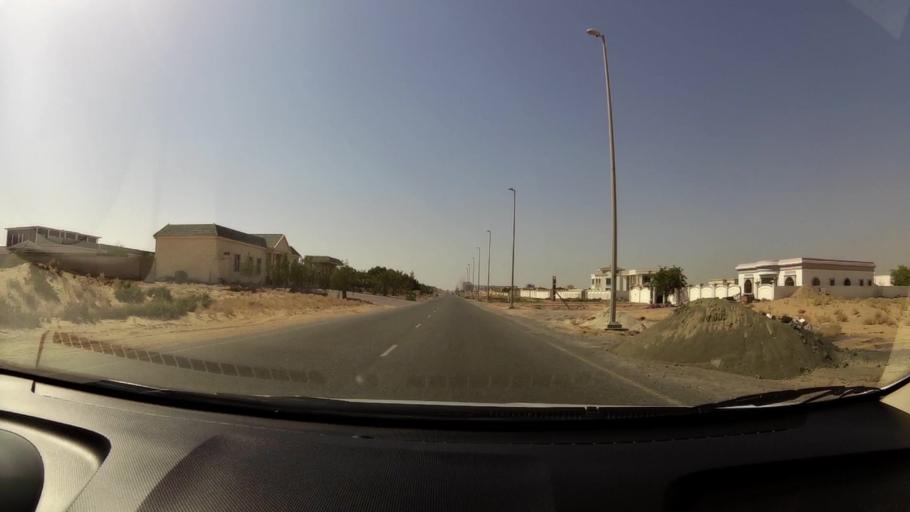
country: AE
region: Umm al Qaywayn
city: Umm al Qaywayn
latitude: 25.4830
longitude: 55.6028
